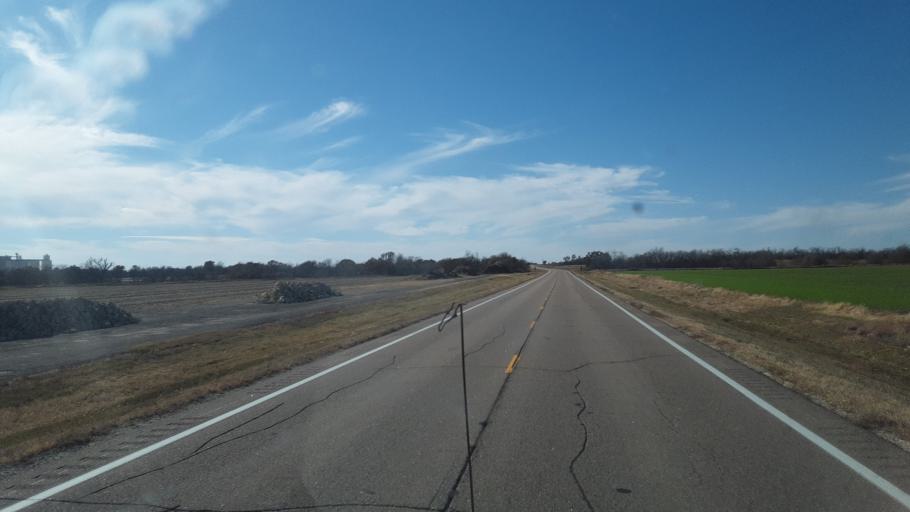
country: US
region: Kansas
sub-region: Pawnee County
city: Larned
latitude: 38.1896
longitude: -99.2970
